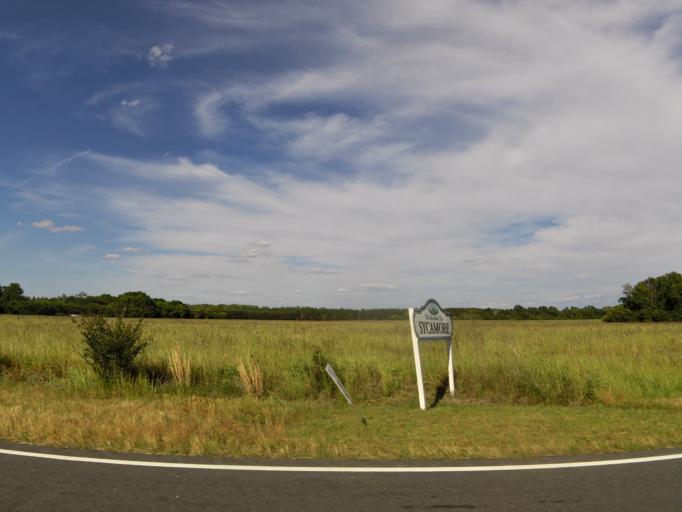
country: US
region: South Carolina
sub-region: Allendale County
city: Fairfax
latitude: 33.0231
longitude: -81.2192
